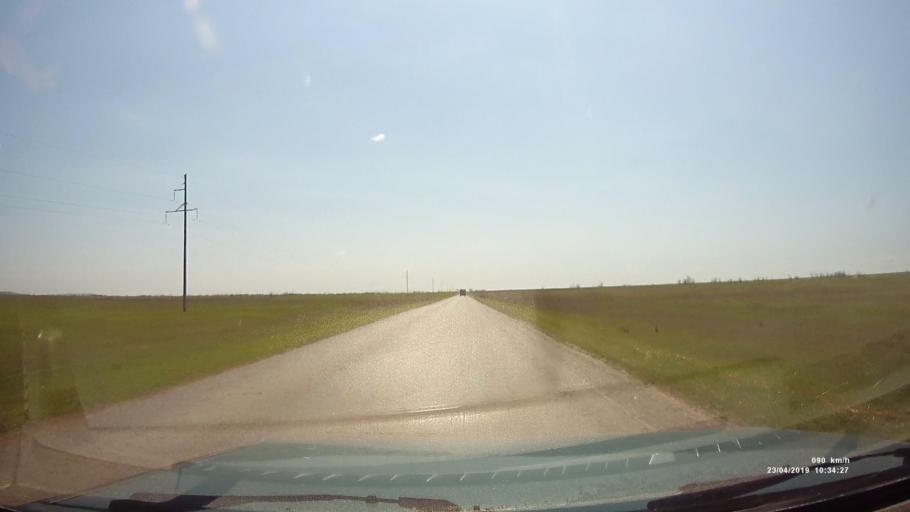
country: RU
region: Kalmykiya
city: Yashalta
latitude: 46.5638
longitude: 42.6106
